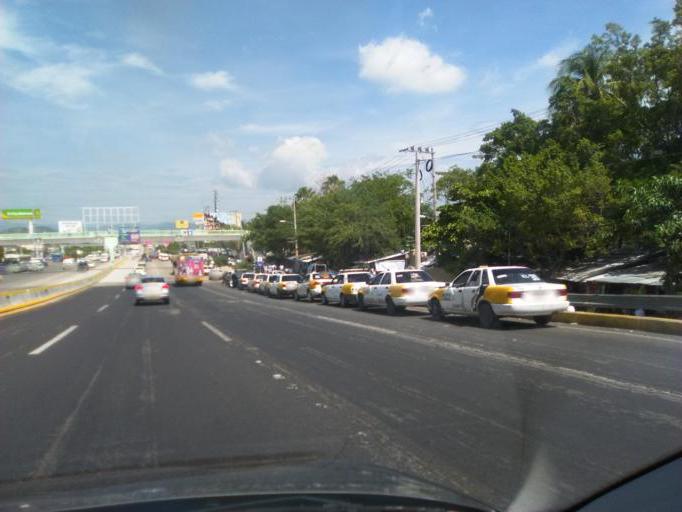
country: MX
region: Guerrero
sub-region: Acapulco de Juarez
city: Colonia Alborada
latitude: 16.8883
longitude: -99.8370
